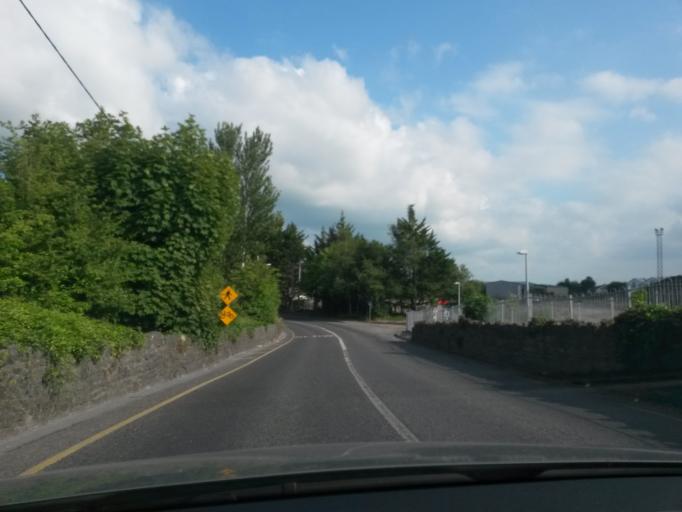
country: IE
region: Munster
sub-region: An Clar
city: Ennis
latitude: 52.8402
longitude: -8.9748
